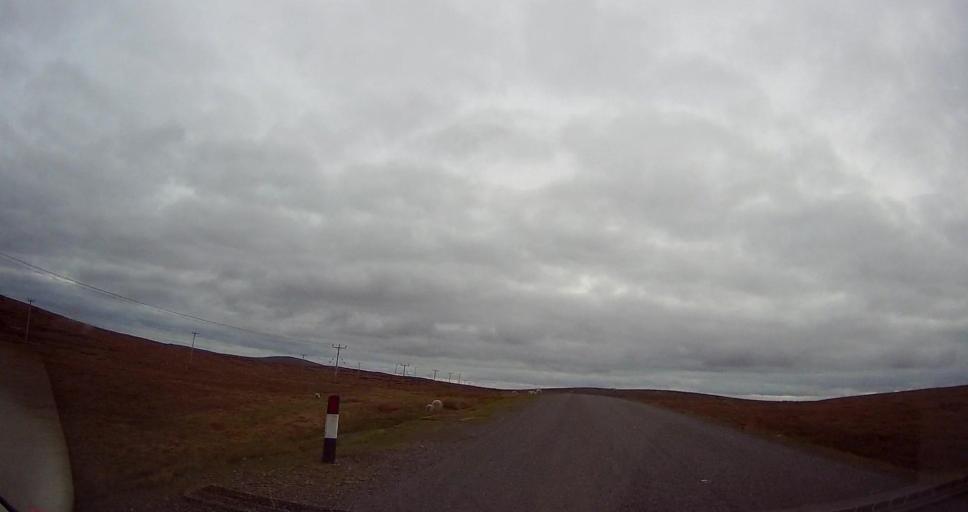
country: GB
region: Scotland
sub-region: Shetland Islands
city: Shetland
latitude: 60.6298
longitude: -1.0678
